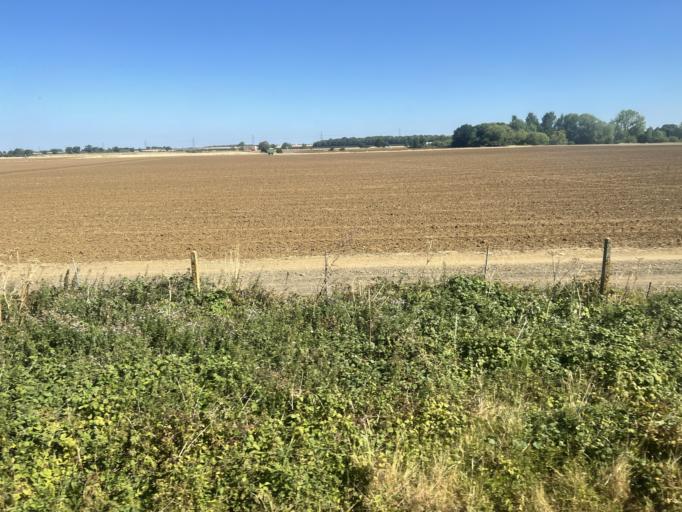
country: GB
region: England
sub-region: Lincolnshire
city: Heckington
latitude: 52.9884
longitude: -0.3517
